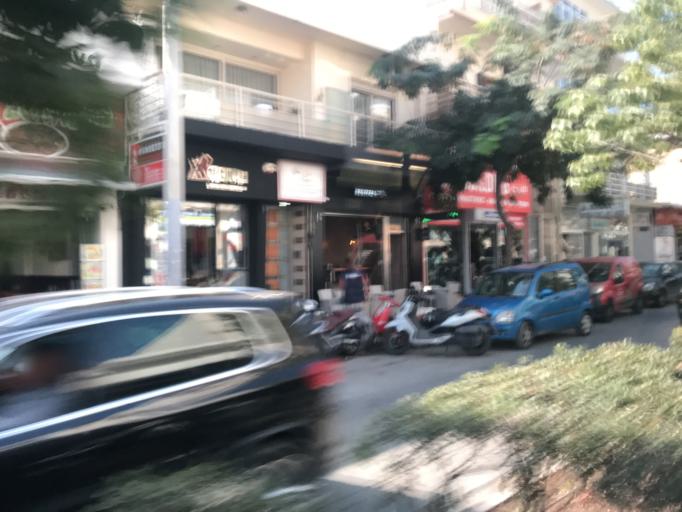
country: GR
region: Crete
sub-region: Nomos Irakleiou
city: Irakleion
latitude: 35.3364
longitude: 25.1234
